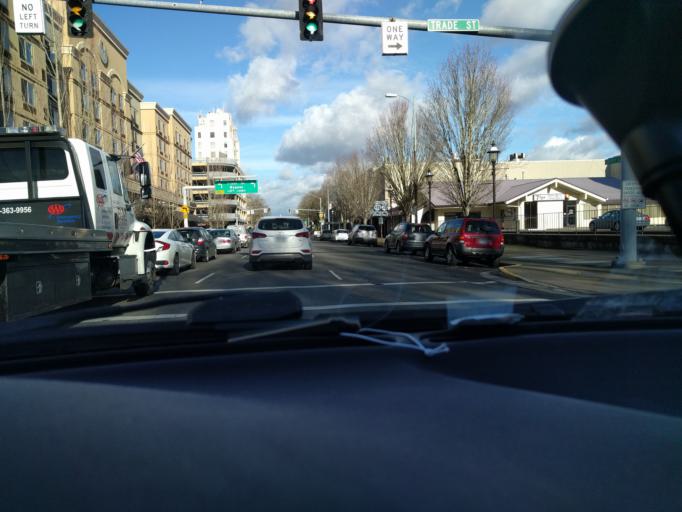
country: US
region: Oregon
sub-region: Marion County
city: Salem
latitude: 44.9381
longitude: -123.0399
